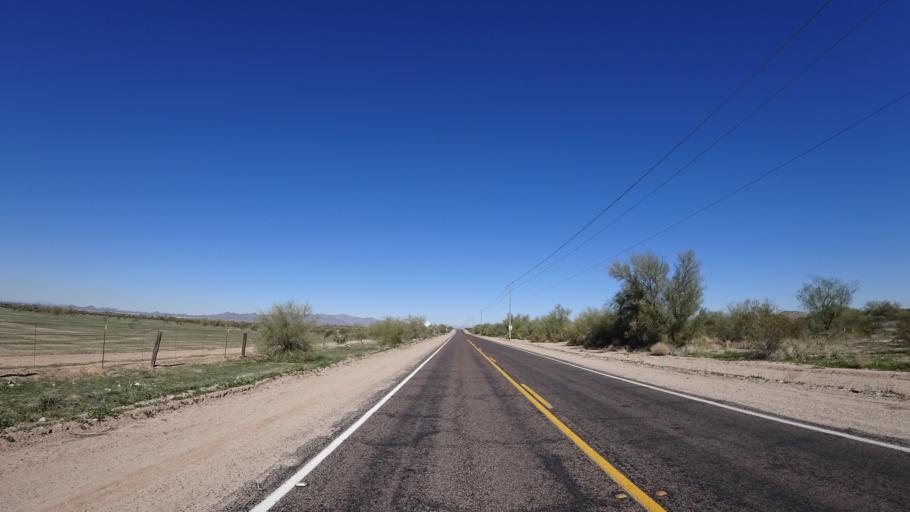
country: US
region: Arizona
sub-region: Maricopa County
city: Buckeye
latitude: 33.3349
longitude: -112.4699
